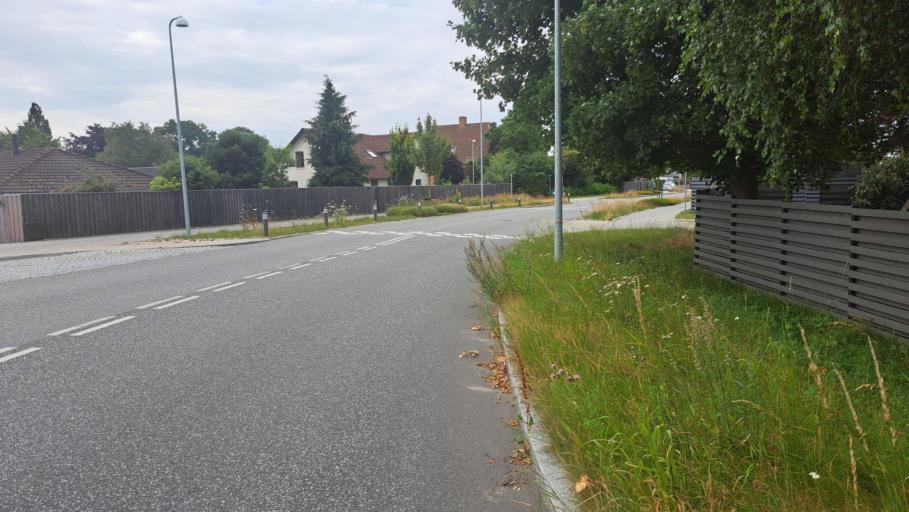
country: DK
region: Central Jutland
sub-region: Hedensted Kommune
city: Hedensted
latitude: 55.7747
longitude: 9.7082
